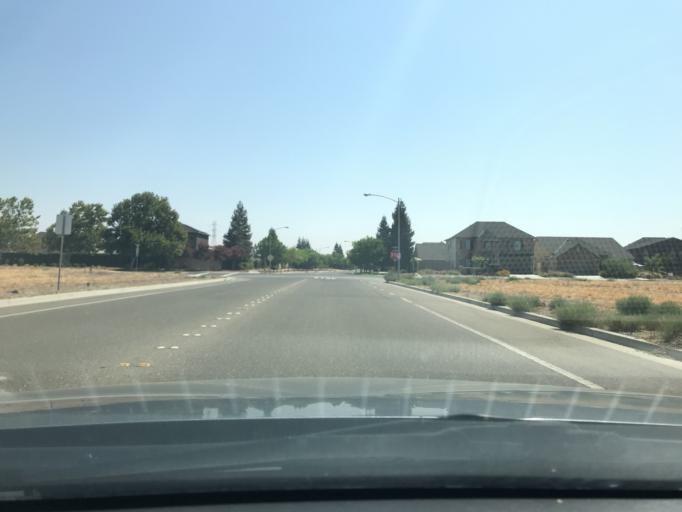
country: US
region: California
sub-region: Merced County
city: Merced
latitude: 37.3582
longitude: -120.4739
